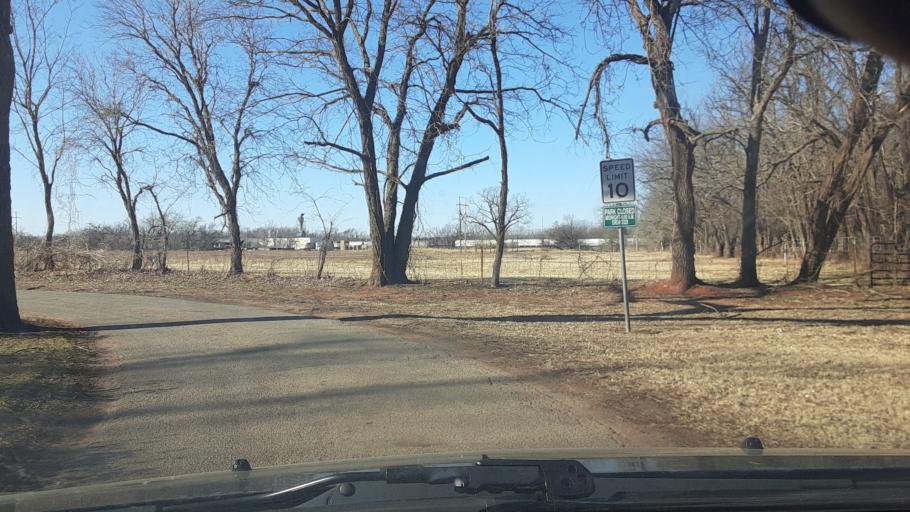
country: US
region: Oklahoma
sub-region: Logan County
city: Guthrie
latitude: 35.8706
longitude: -97.4283
